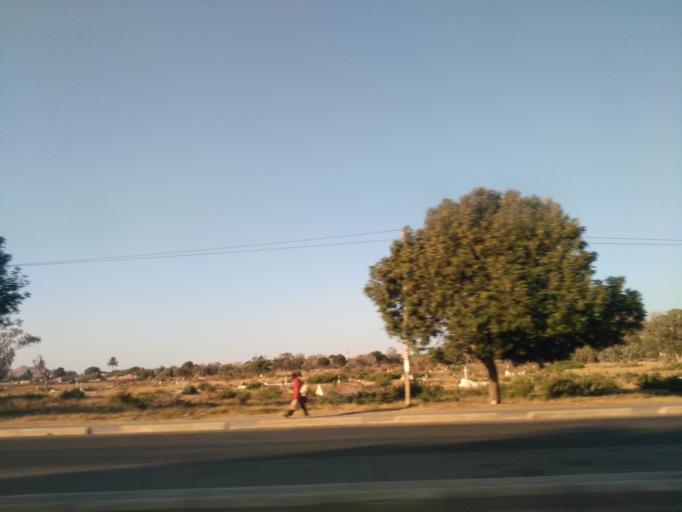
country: TZ
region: Dodoma
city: Dodoma
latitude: -6.1741
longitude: 35.7364
